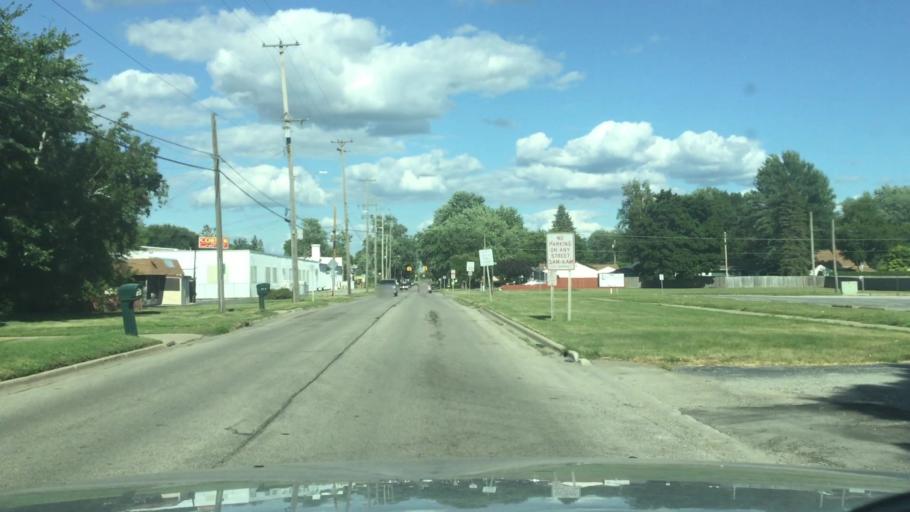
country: US
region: Michigan
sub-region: Saginaw County
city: Saginaw
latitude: 43.4007
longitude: -83.9951
